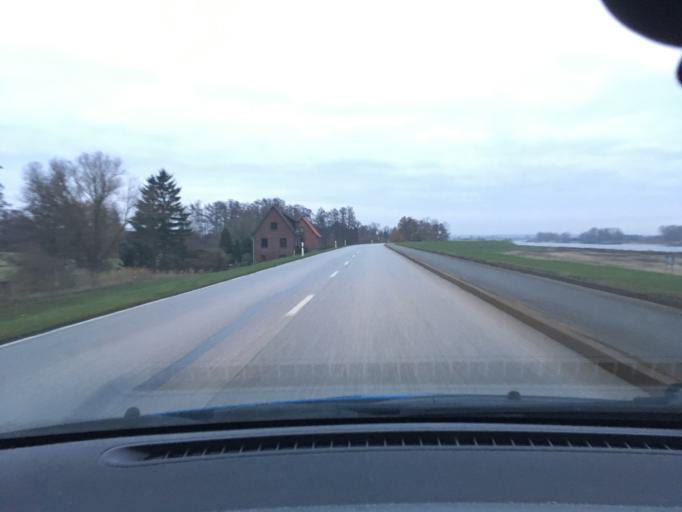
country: DE
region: Lower Saxony
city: Drage
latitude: 53.4009
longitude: 10.2402
